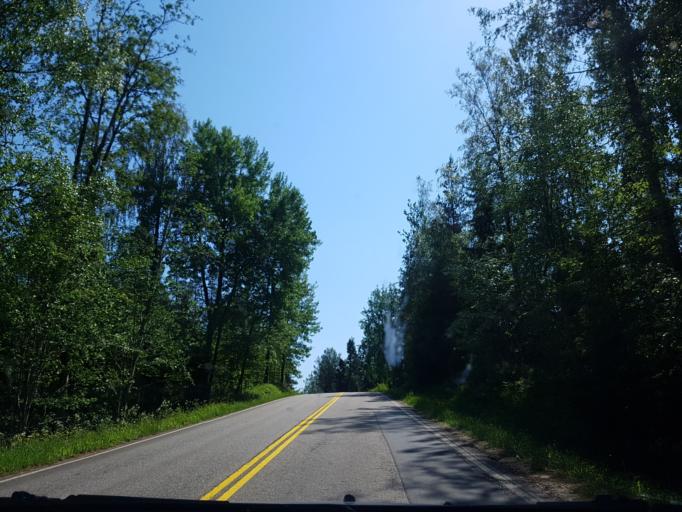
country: FI
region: Uusimaa
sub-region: Helsinki
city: Vihti
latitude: 60.3031
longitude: 24.4002
